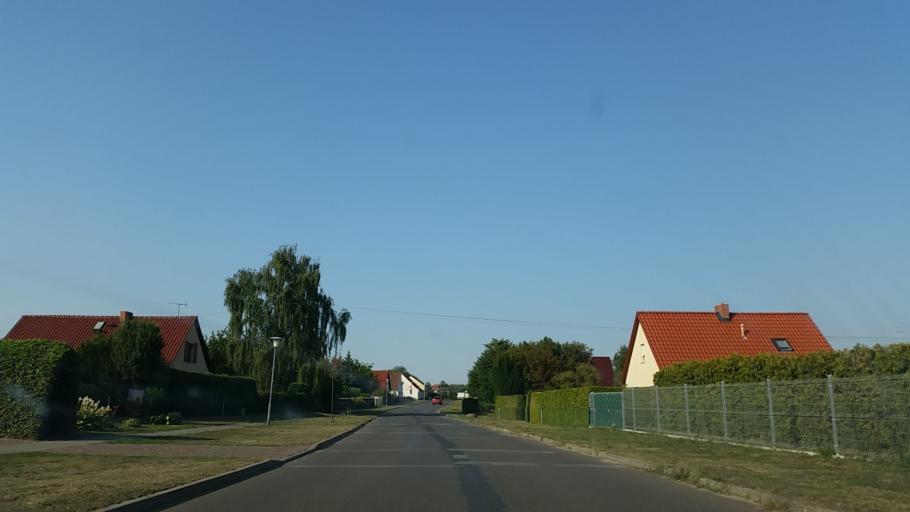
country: DE
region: Brandenburg
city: Pinnow
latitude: 53.0025
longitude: 14.0823
